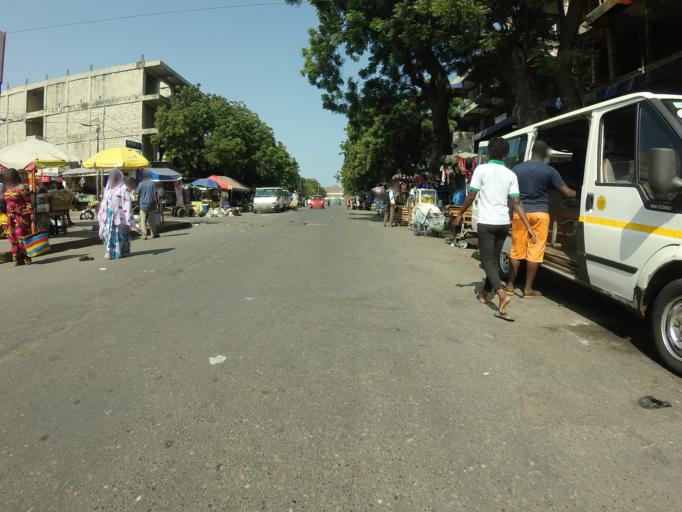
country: GH
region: Greater Accra
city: Accra
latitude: 5.5505
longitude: -0.2065
